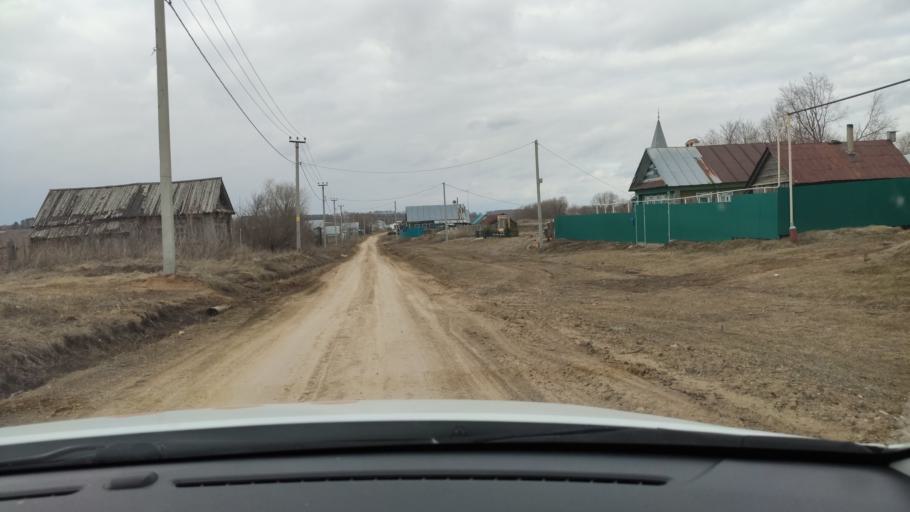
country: RU
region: Tatarstan
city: Vysokaya Gora
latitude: 56.2124
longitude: 49.3132
